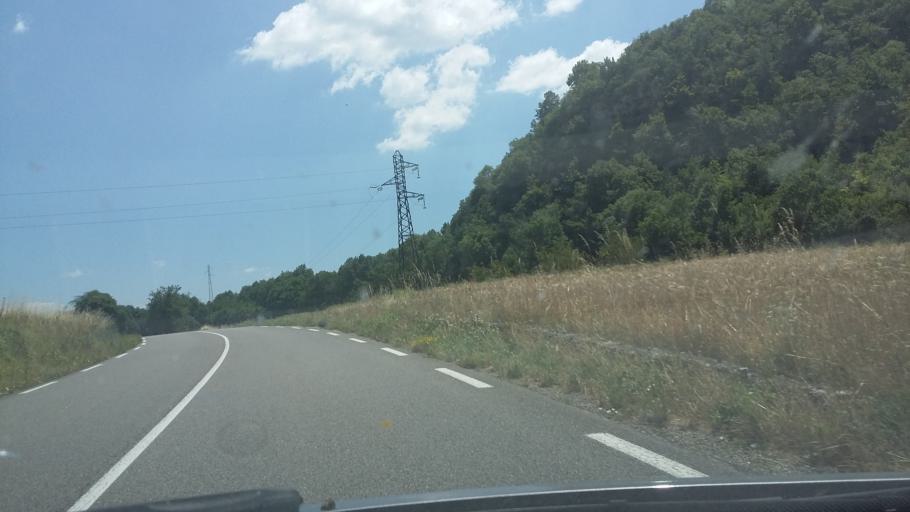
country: FR
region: Rhone-Alpes
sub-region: Departement de l'Ain
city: Virieu-le-Grand
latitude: 45.8263
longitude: 5.5980
